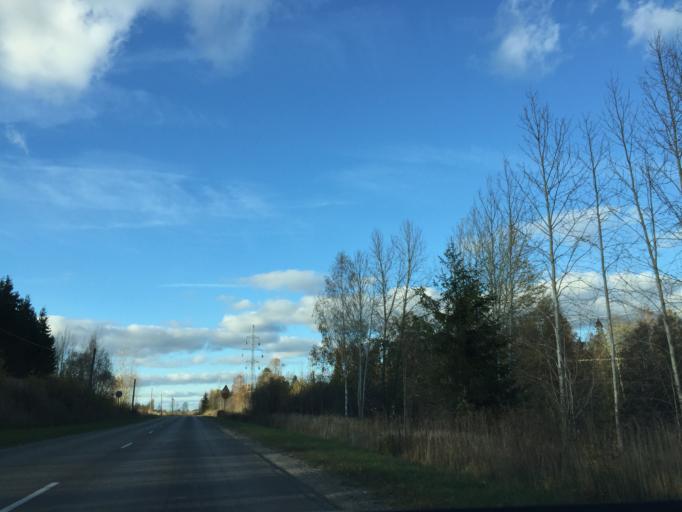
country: LV
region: Tukuma Rajons
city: Tukums
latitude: 56.9766
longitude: 23.1191
